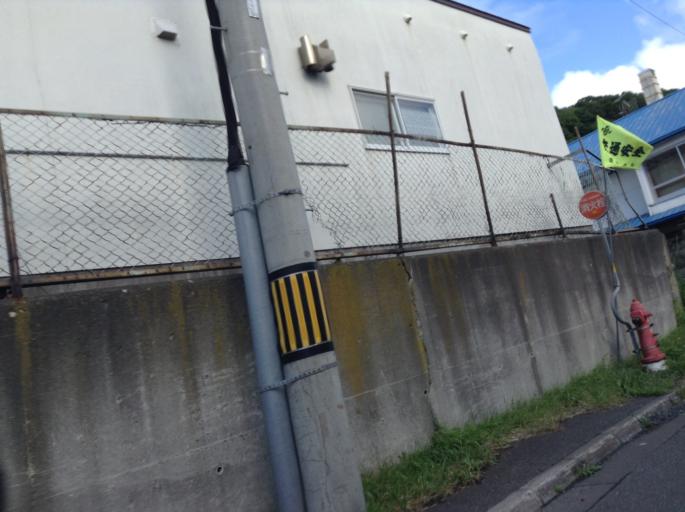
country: JP
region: Hokkaido
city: Wakkanai
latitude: 45.4059
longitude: 141.6746
